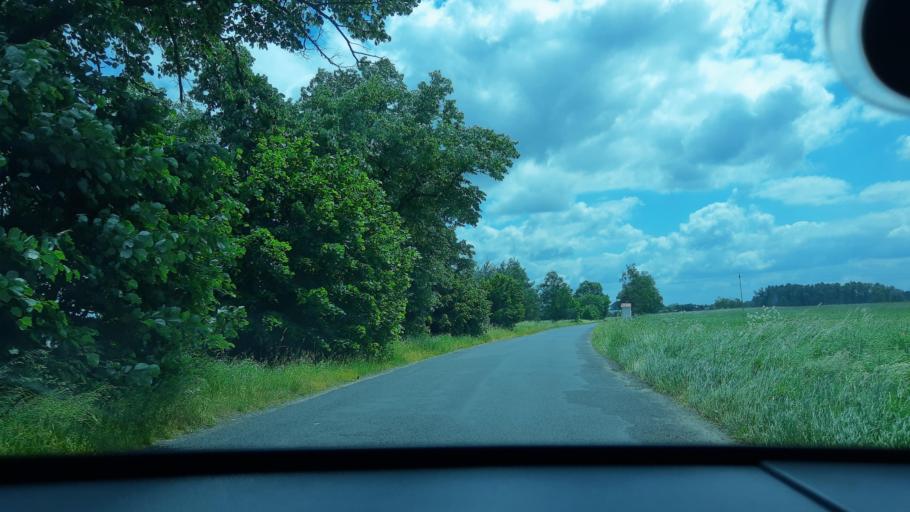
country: PL
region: Lodz Voivodeship
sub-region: Powiat zdunskowolski
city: Zapolice
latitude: 51.5393
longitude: 18.8228
